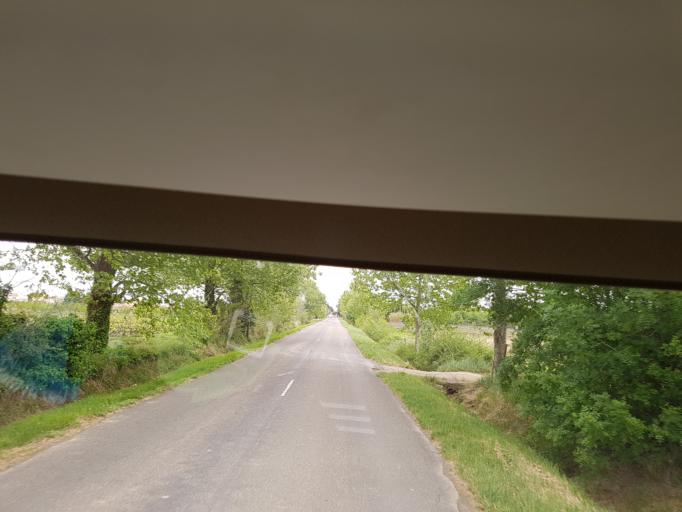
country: FR
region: Languedoc-Roussillon
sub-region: Departement des Pyrenees-Orientales
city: Baho
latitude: 42.7040
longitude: 2.8123
